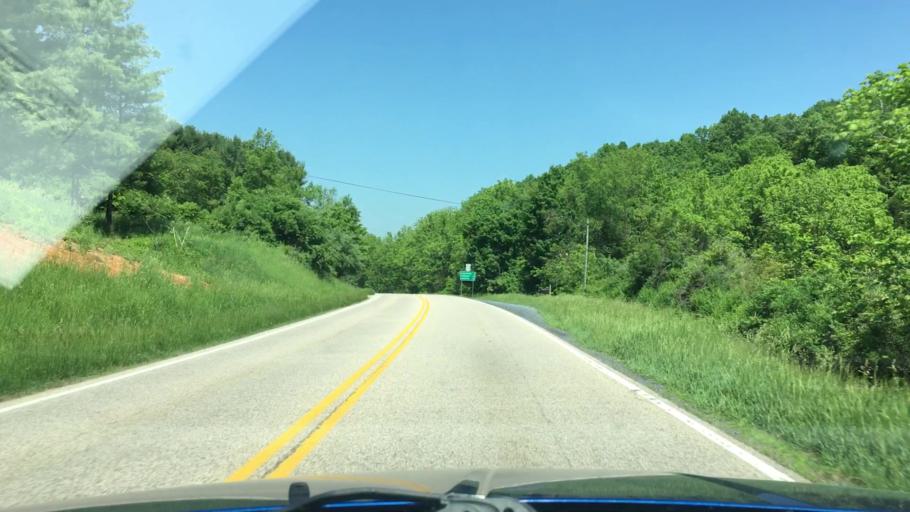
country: US
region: Virginia
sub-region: City of Staunton
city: Staunton
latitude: 38.1882
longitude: -79.1039
